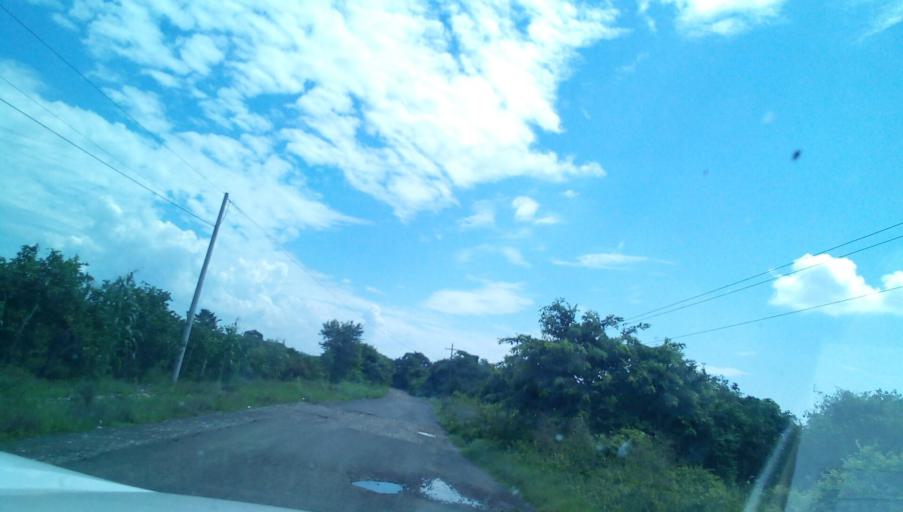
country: MX
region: Veracruz
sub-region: Alamo Temapache
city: Vegas de la Soledad y Soledad Dos
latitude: 20.9047
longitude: -97.9338
